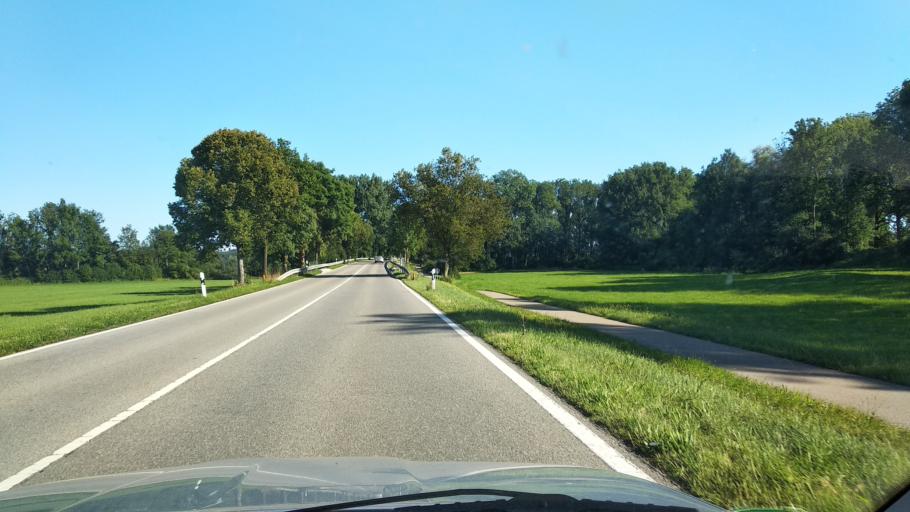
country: DE
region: Baden-Wuerttemberg
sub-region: Tuebingen Region
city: Leutkirch im Allgau
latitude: 47.7988
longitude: 10.0392
